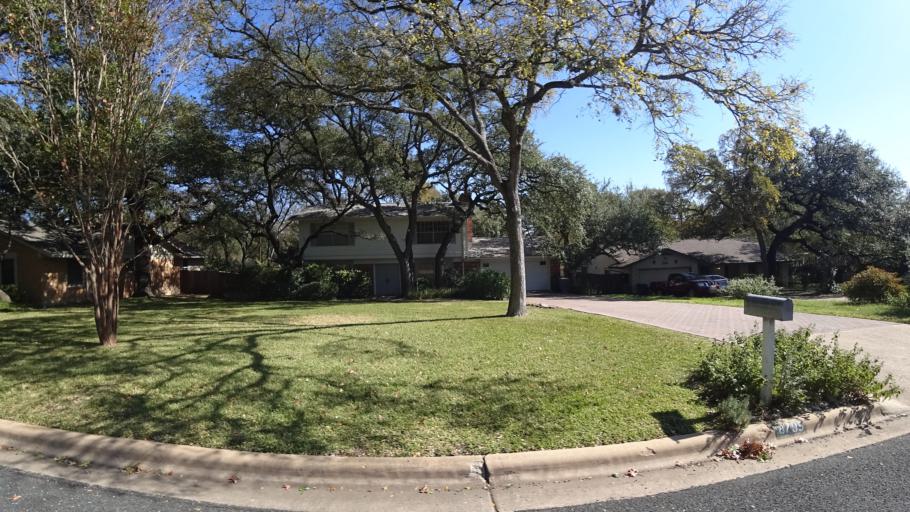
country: US
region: Texas
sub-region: Williamson County
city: Jollyville
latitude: 30.3779
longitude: -97.7449
